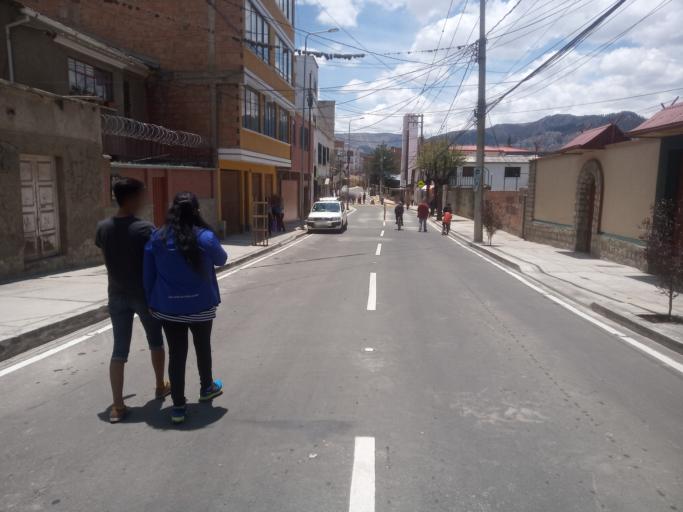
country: BO
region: La Paz
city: La Paz
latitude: -16.5119
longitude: -68.1340
